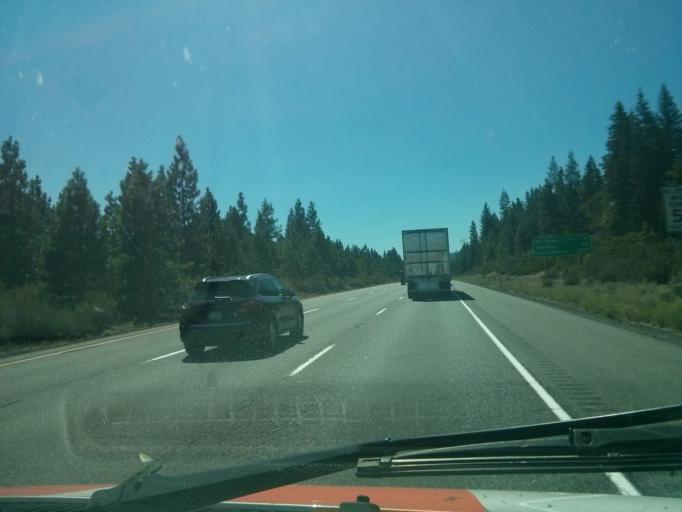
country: US
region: California
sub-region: Siskiyou County
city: Weed
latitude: 41.3869
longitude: -122.3760
